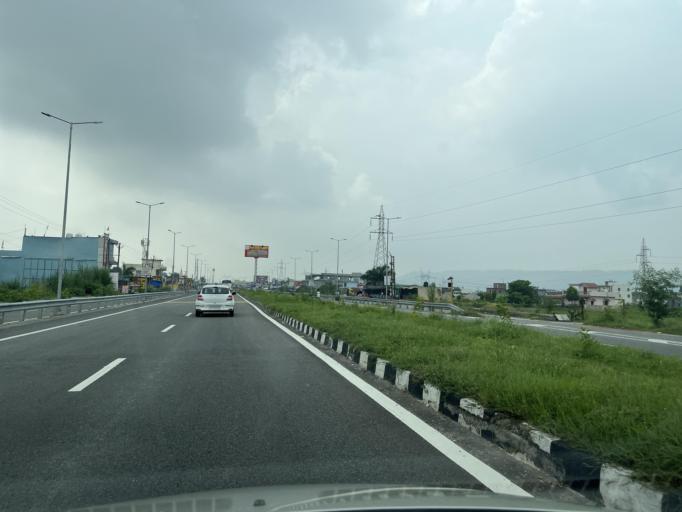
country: IN
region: Uttarakhand
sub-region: Dehradun
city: Raiwala
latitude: 30.0833
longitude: 78.1898
